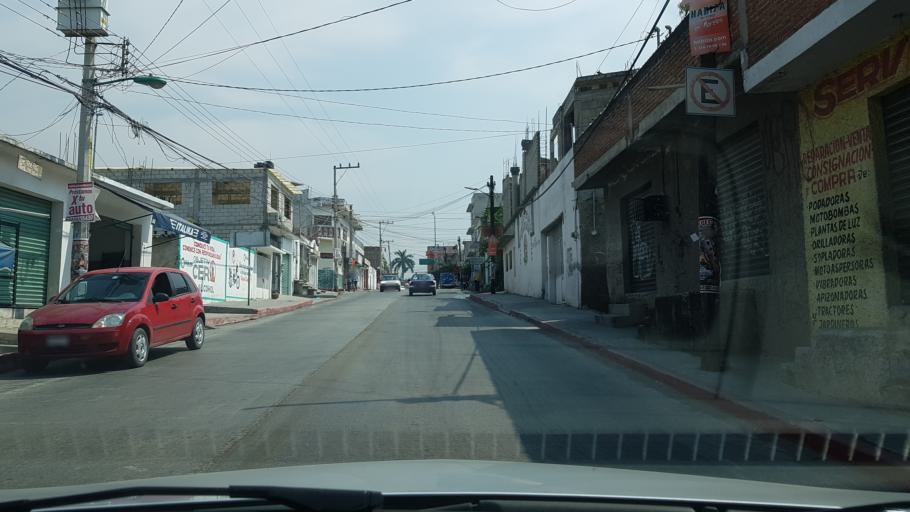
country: MX
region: Morelos
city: Emiliano Zapata
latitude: 18.8362
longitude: -99.1837
